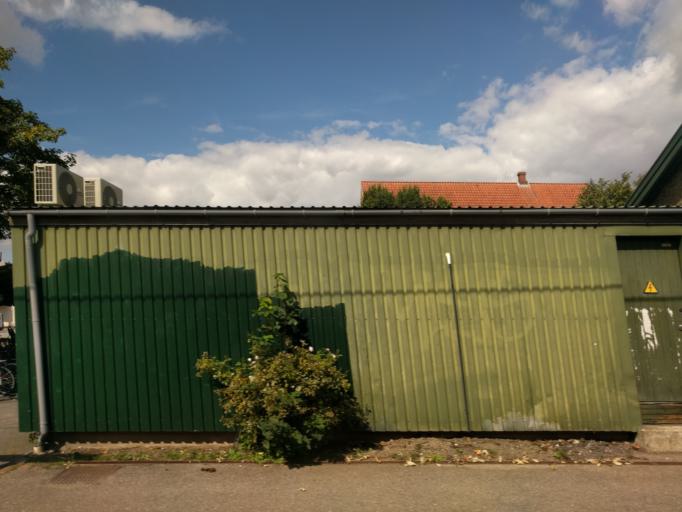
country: DK
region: Zealand
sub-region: Soro Kommune
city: Frederiksberg
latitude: 55.4190
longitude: 11.5684
